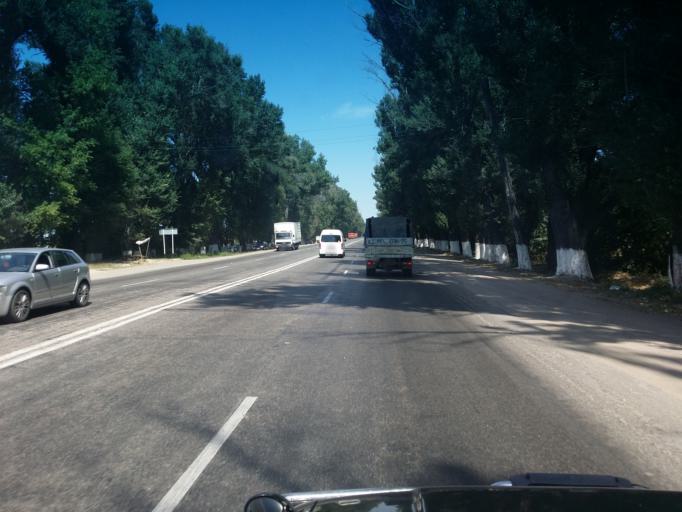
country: KZ
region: Almaty Oblysy
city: Energeticheskiy
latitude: 43.3552
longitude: 77.0697
